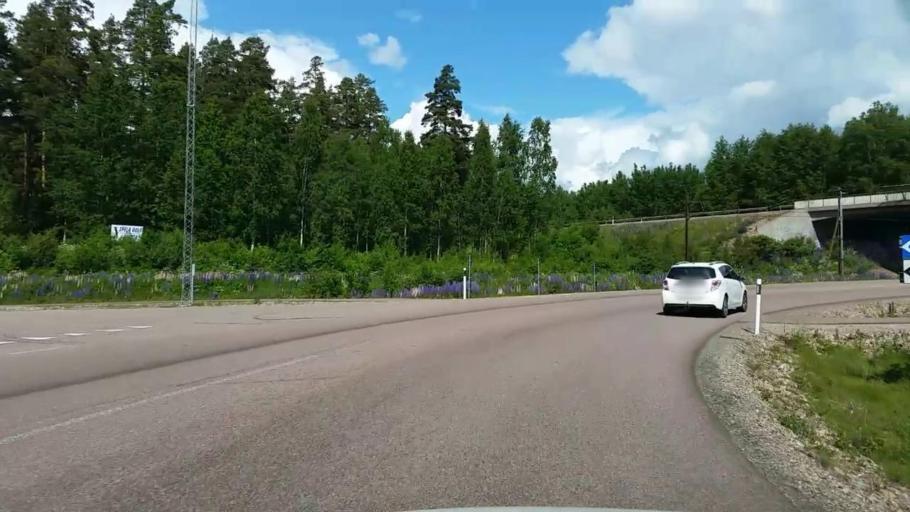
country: SE
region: Dalarna
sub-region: Avesta Kommun
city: Avesta
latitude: 60.1452
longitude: 16.2276
